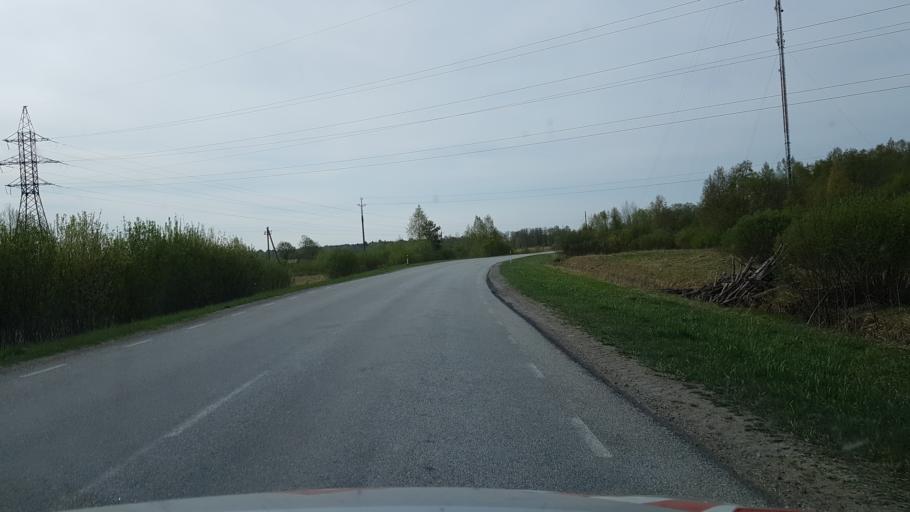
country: EE
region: Paernumaa
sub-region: Audru vald
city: Audru
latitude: 58.4186
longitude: 24.3111
